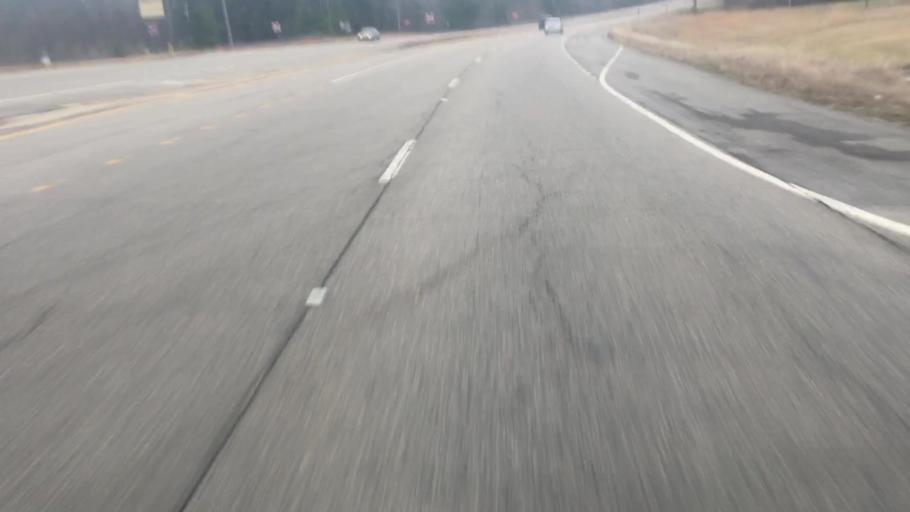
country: US
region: Alabama
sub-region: Walker County
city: Cordova
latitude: 33.8198
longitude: -87.1533
